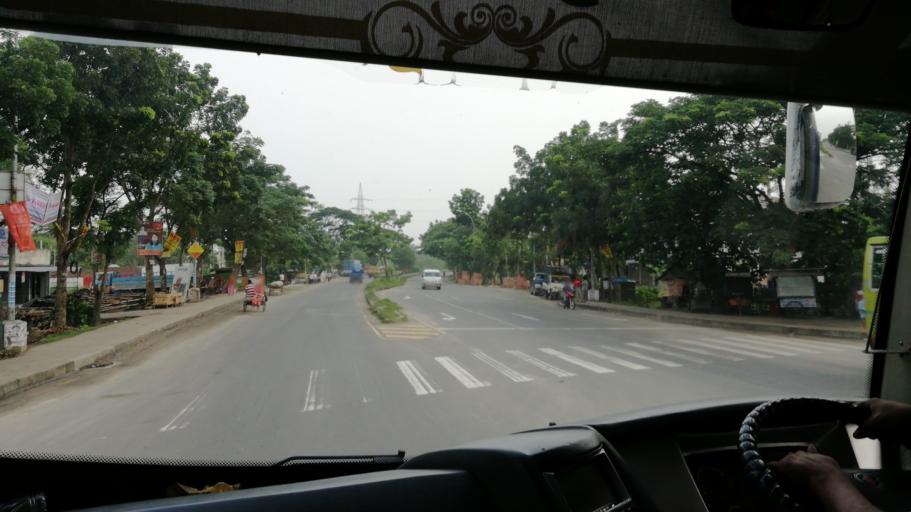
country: BD
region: Khulna
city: Khulna
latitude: 22.7861
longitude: 89.5368
